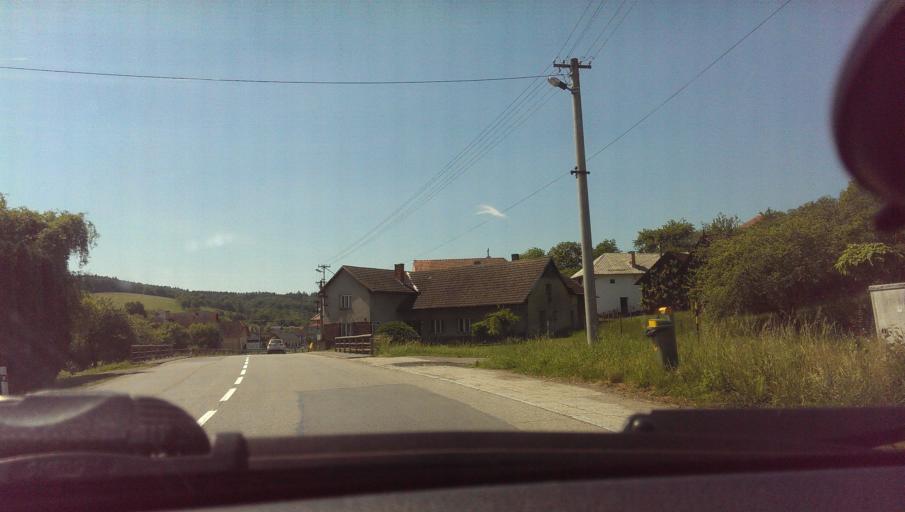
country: CZ
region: Zlin
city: Breznice
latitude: 49.1667
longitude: 17.6390
